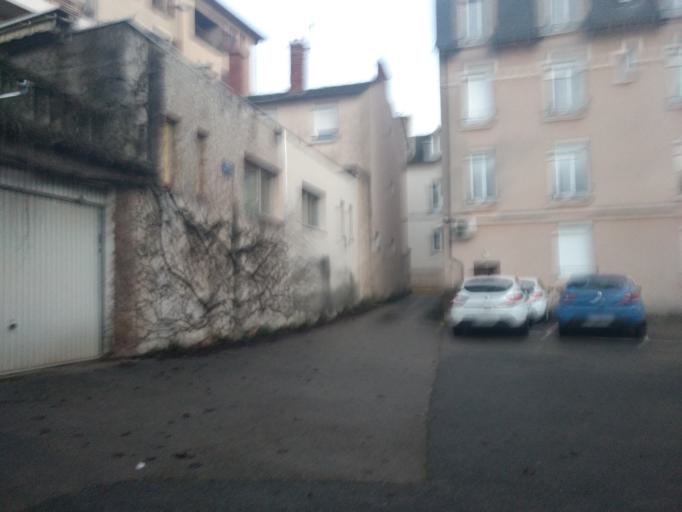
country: FR
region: Midi-Pyrenees
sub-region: Departement de l'Aveyron
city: Rodez
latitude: 44.3466
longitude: 2.5732
